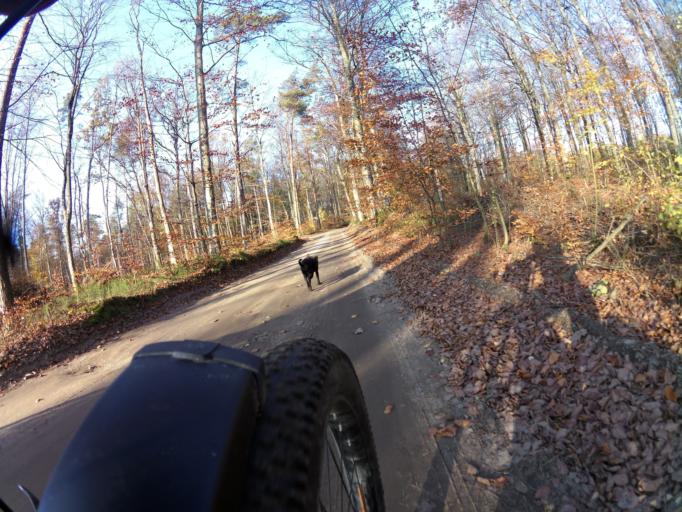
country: PL
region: Pomeranian Voivodeship
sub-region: Powiat pucki
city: Krokowa
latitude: 54.7285
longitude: 18.2073
